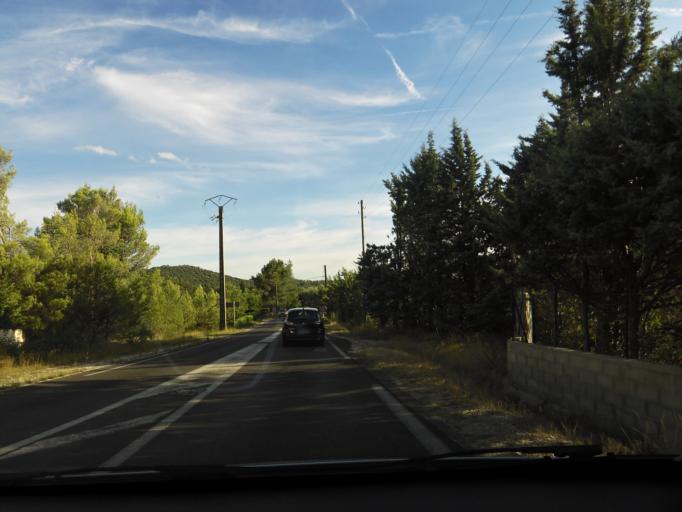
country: FR
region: Languedoc-Roussillon
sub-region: Departement de l'Herault
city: Saint-Mathieu-de-Treviers
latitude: 43.8095
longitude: 3.8873
